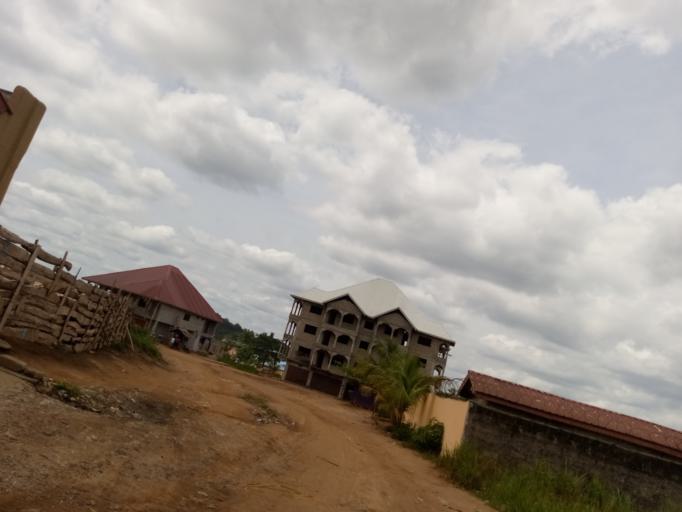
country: SL
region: Western Area
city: Waterloo
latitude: 8.3318
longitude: -13.0298
